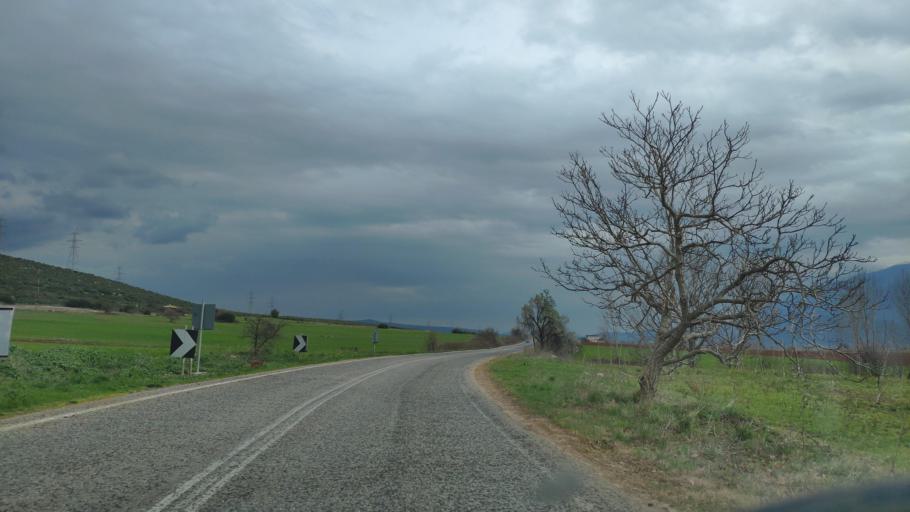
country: GR
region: Central Greece
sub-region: Nomos Fthiotidos
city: Amfikleia
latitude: 38.7063
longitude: 22.5019
